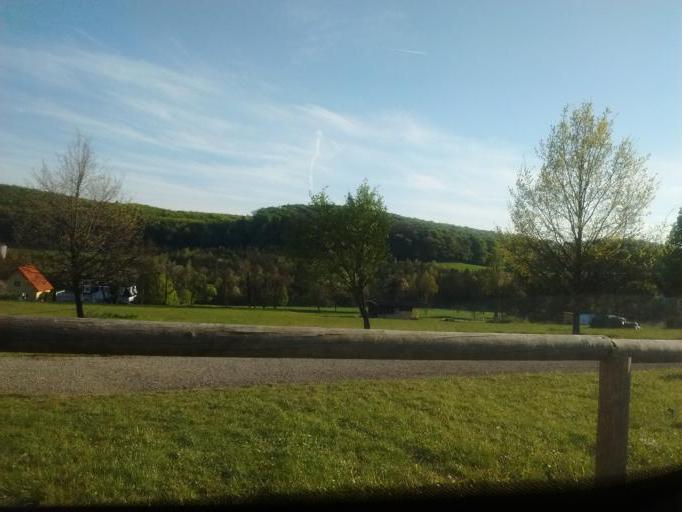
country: AT
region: Lower Austria
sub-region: Politischer Bezirk Modling
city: Gaaden
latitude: 48.0760
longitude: 16.1873
